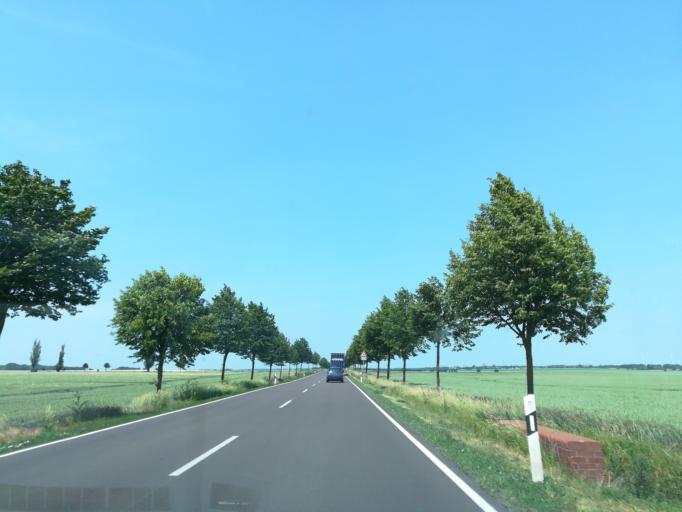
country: DE
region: Saxony-Anhalt
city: Schneidlingen
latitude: 51.9068
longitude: 11.4336
